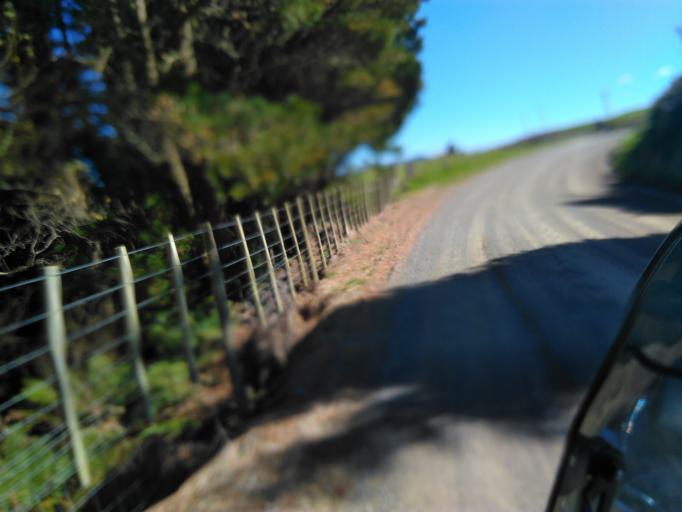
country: NZ
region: Bay of Plenty
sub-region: Opotiki District
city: Opotiki
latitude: -38.3108
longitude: 177.5646
